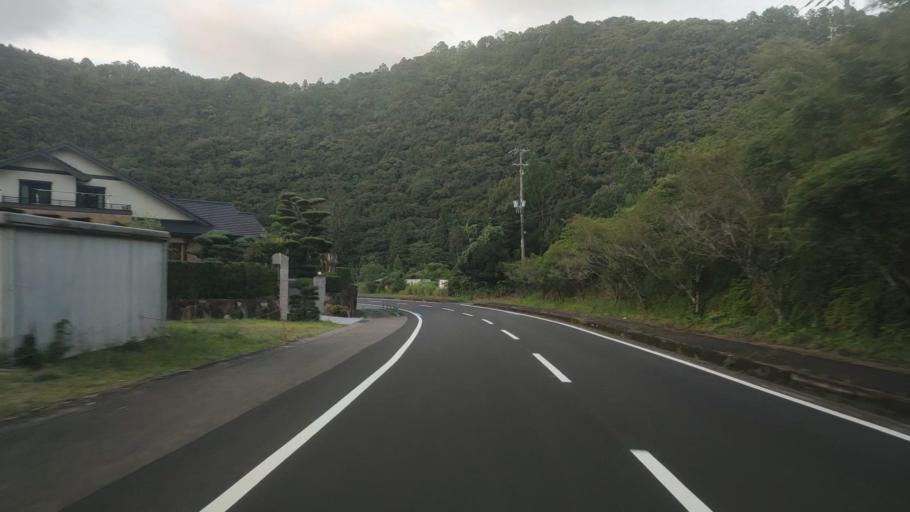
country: JP
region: Wakayama
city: Shingu
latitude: 33.8226
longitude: 135.7757
